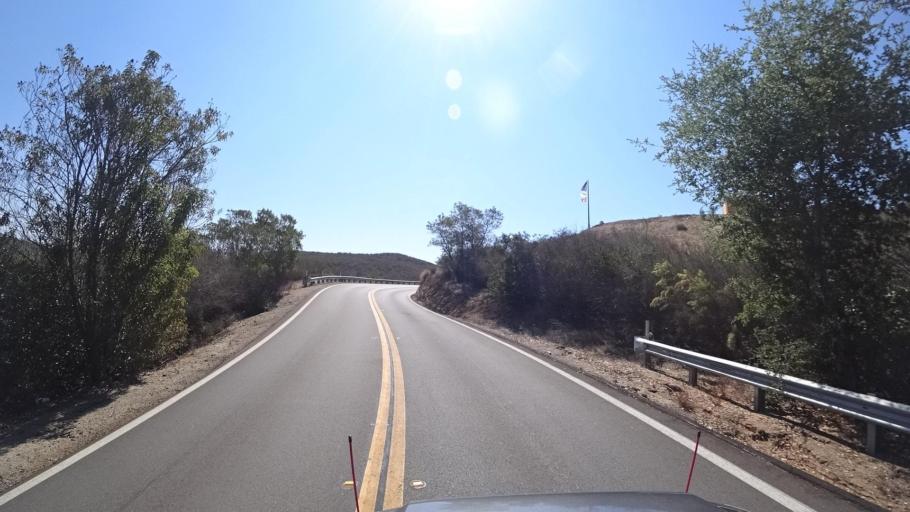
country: US
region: California
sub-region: San Diego County
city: Harbison Canyon
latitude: 32.8274
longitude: -116.8368
